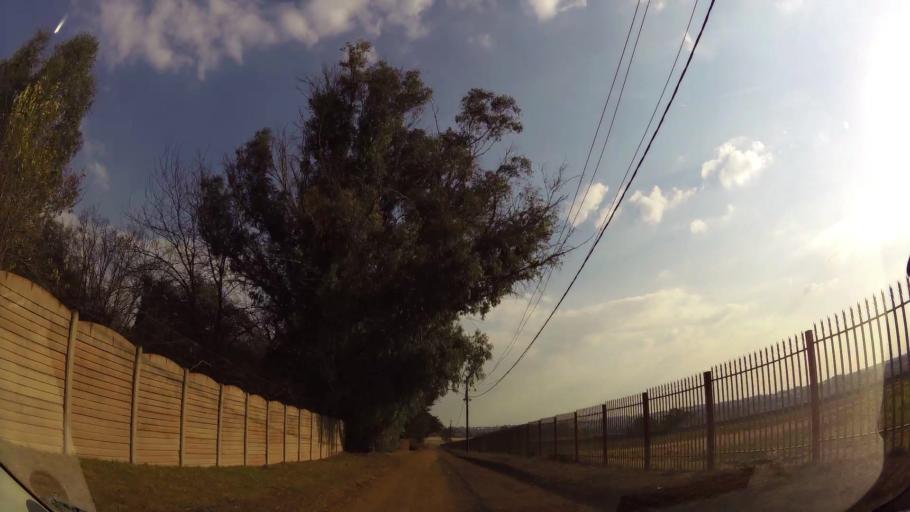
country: ZA
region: Gauteng
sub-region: Ekurhuleni Metropolitan Municipality
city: Benoni
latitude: -26.0937
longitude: 28.2882
